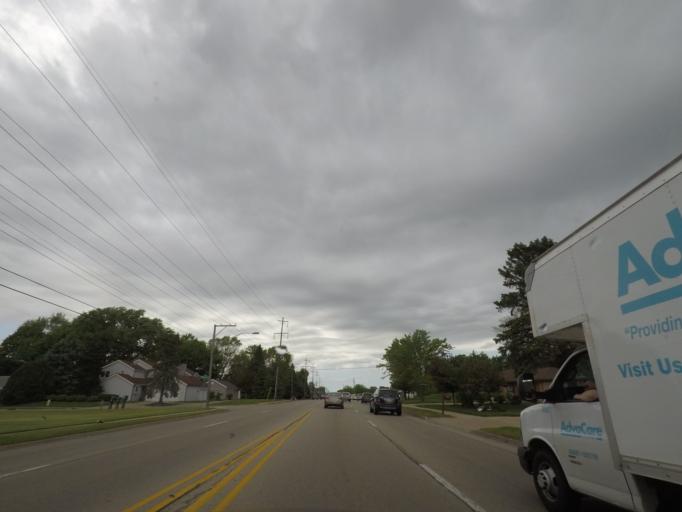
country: US
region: Illinois
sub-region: Winnebago County
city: Loves Park
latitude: 42.2776
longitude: -89.0290
